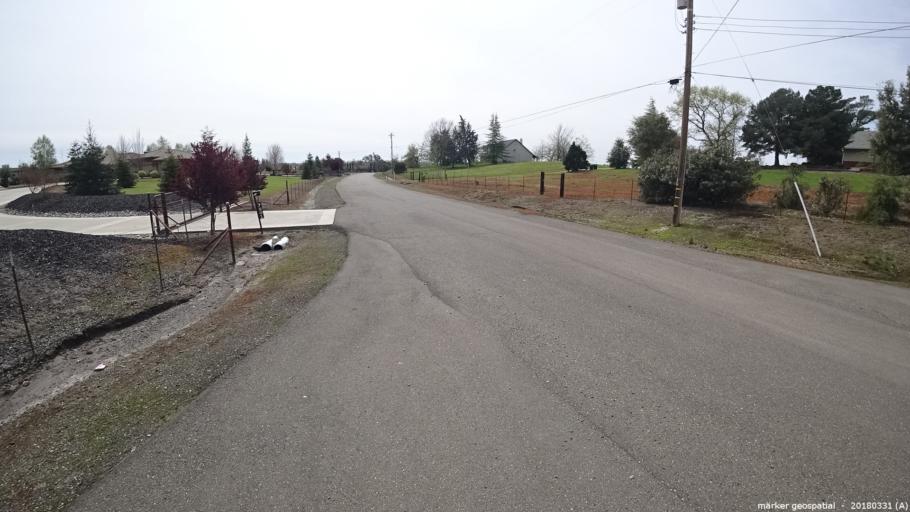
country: US
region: California
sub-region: Sacramento County
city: Rancho Murieta
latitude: 38.5017
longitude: -121.1099
